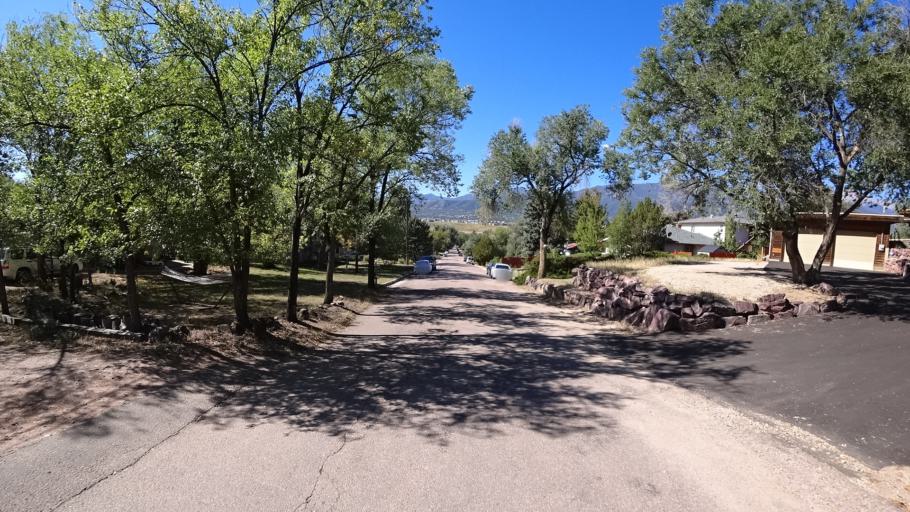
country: US
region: Colorado
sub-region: El Paso County
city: Colorado Springs
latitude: 38.8420
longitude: -104.8434
